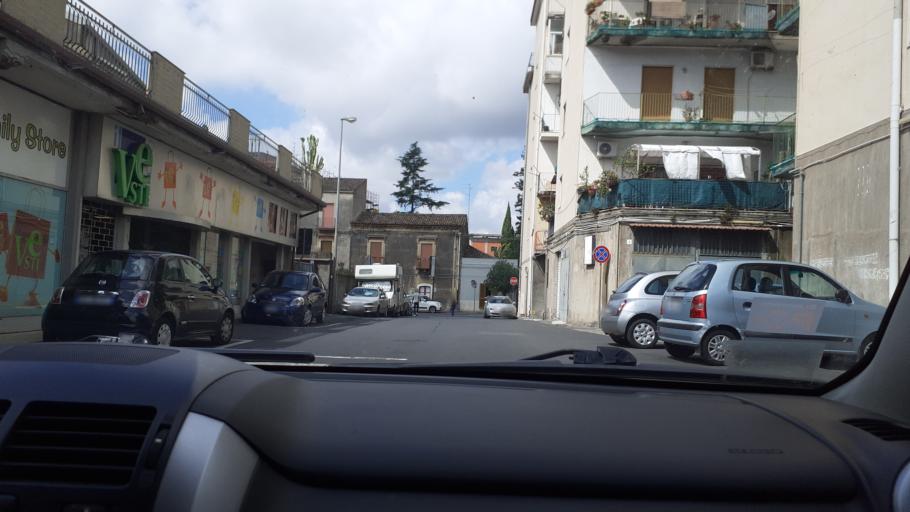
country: IT
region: Sicily
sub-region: Catania
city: San Giovanni la Punta
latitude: 37.5810
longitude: 15.0967
